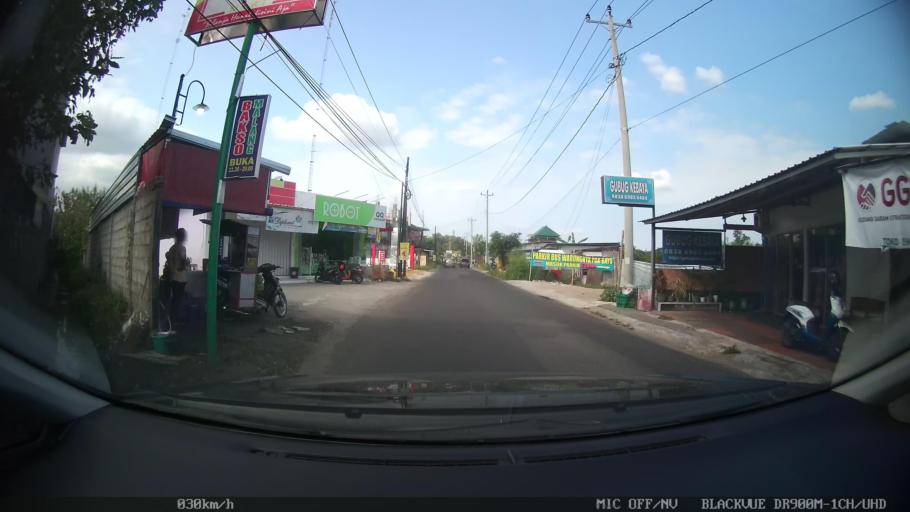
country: ID
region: Daerah Istimewa Yogyakarta
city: Depok
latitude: -7.7299
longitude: 110.4077
